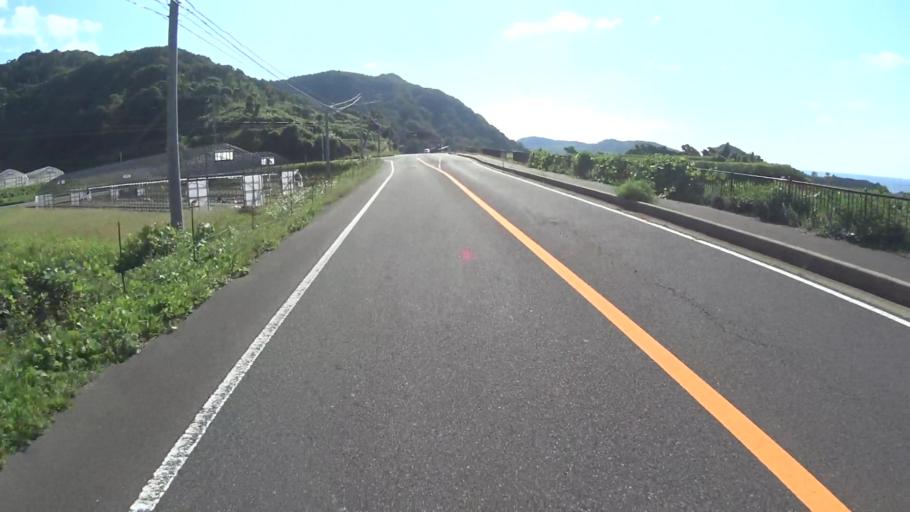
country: JP
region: Kyoto
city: Miyazu
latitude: 35.7442
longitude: 135.1201
